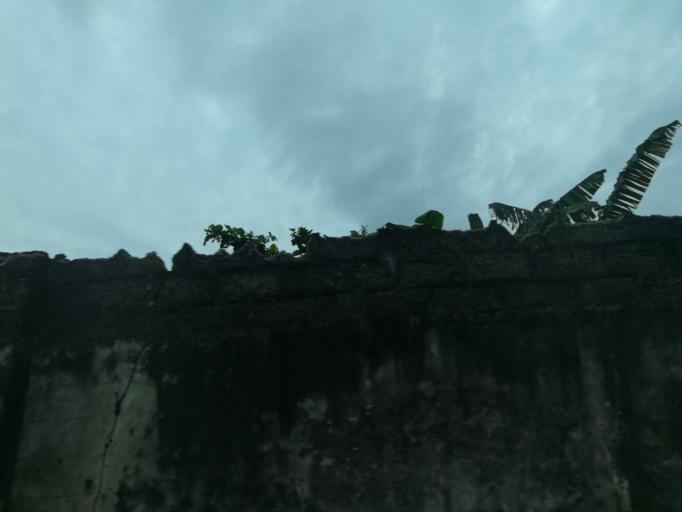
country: NG
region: Rivers
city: Port Harcourt
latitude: 4.8330
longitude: 7.0193
